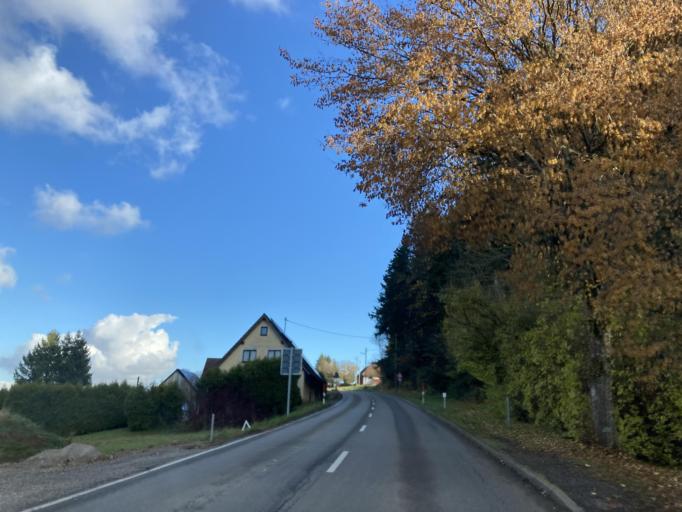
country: DE
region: Baden-Wuerttemberg
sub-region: Freiburg Region
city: Dornhan
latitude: 48.3429
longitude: 8.4635
